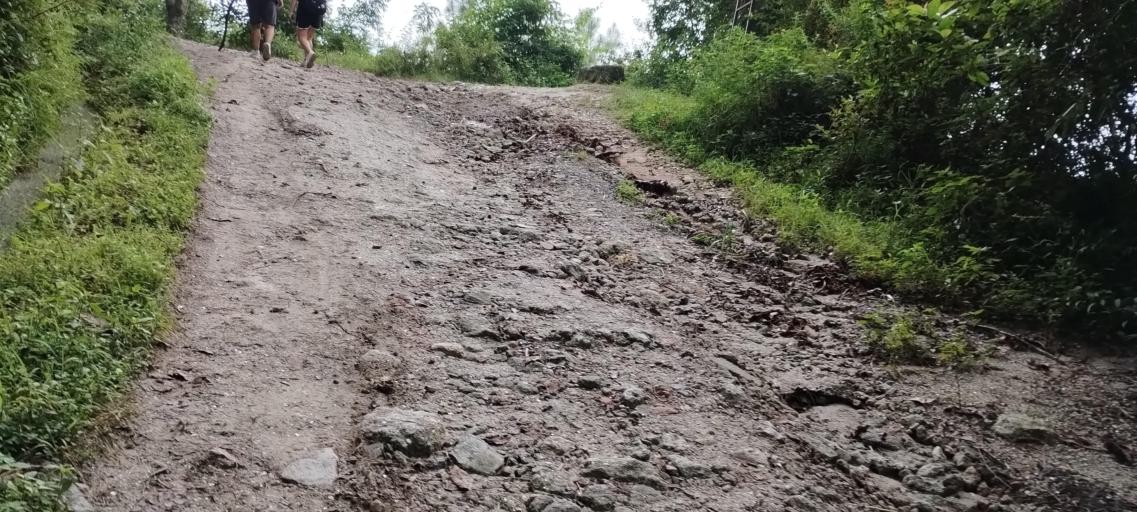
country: NP
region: Central Region
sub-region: Bagmati Zone
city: Kathmandu
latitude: 27.7869
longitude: 85.3739
